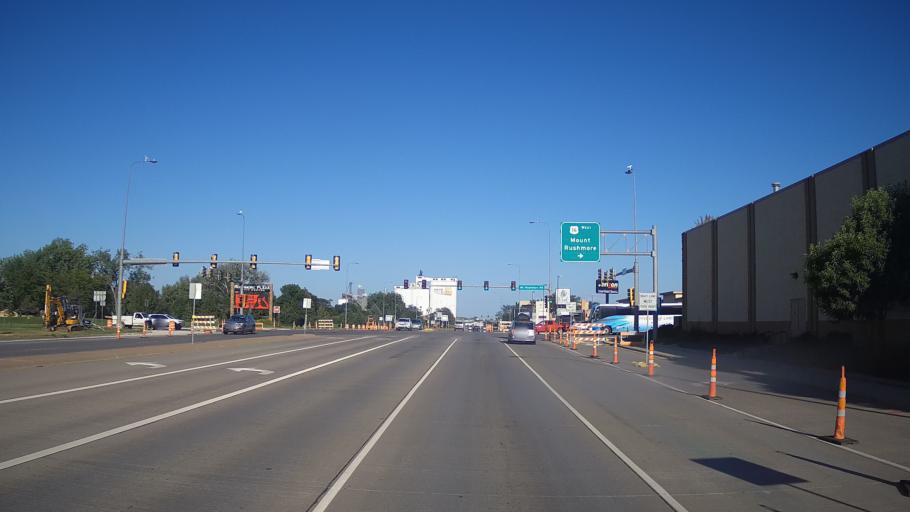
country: US
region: South Dakota
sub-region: Pennington County
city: Rapid City
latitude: 44.0840
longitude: -103.2311
